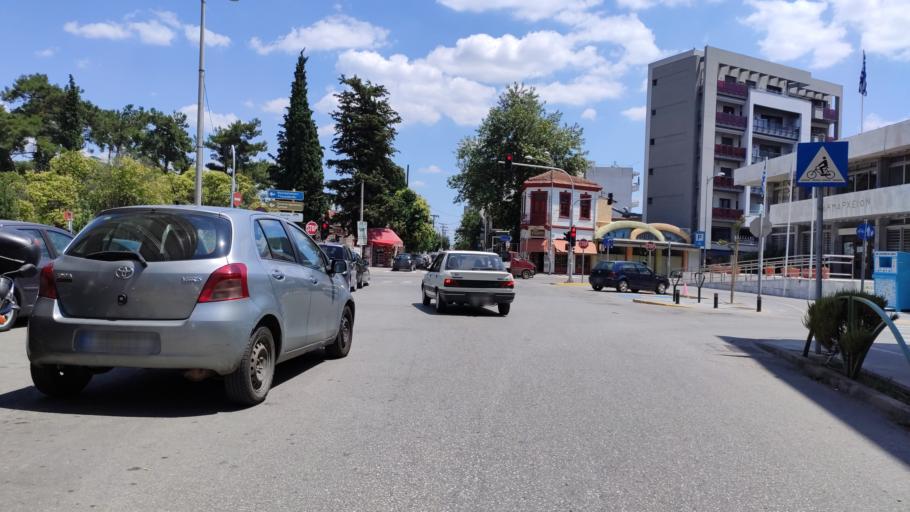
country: GR
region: East Macedonia and Thrace
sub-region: Nomos Rodopis
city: Komotini
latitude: 41.1163
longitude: 25.4062
